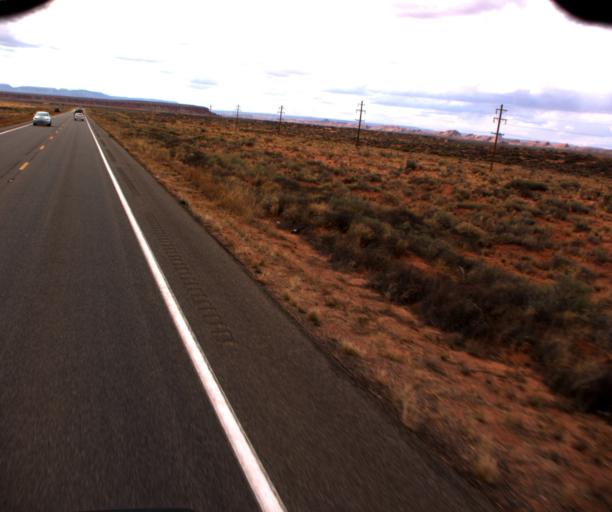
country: US
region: Arizona
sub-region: Navajo County
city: Kayenta
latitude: 36.7920
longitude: -109.9456
